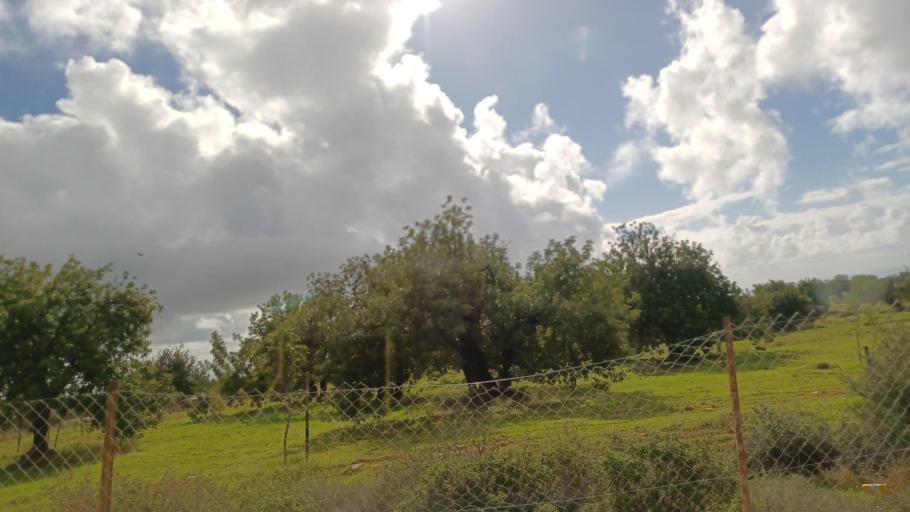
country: CY
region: Limassol
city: Sotira
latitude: 34.7238
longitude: 32.8286
